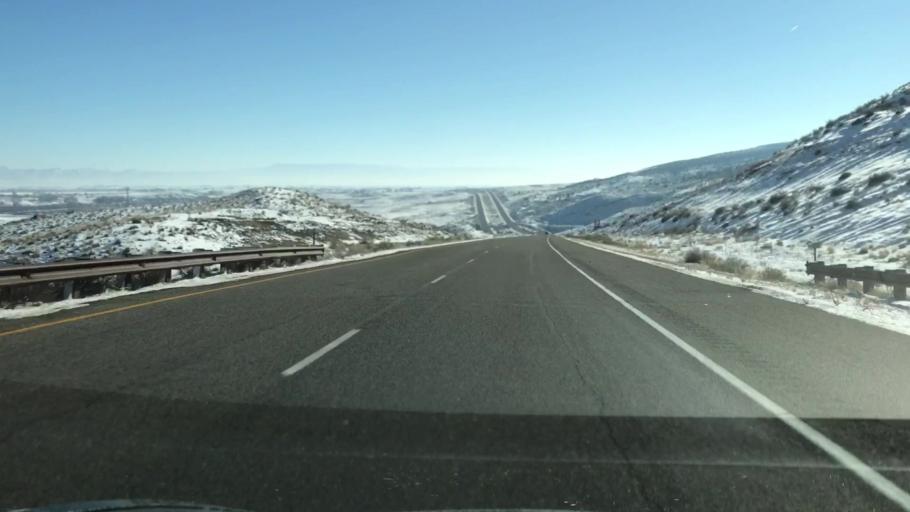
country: US
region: Colorado
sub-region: Mesa County
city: Loma
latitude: 39.2284
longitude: -108.9029
